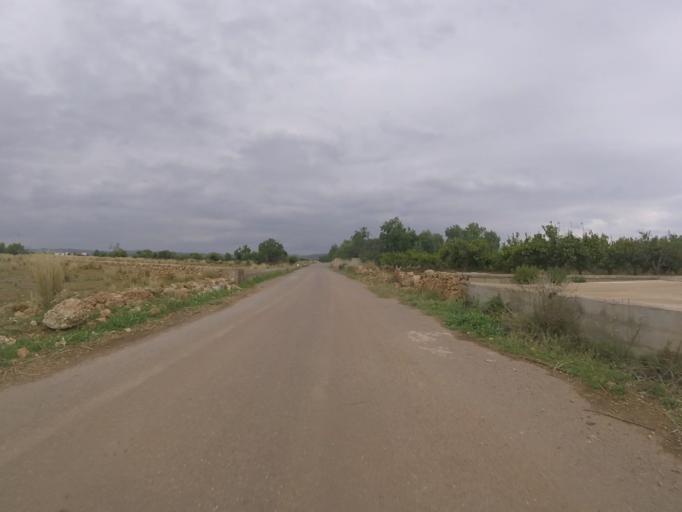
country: ES
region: Valencia
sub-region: Provincia de Castello
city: Torreblanca
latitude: 40.2155
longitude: 0.2341
